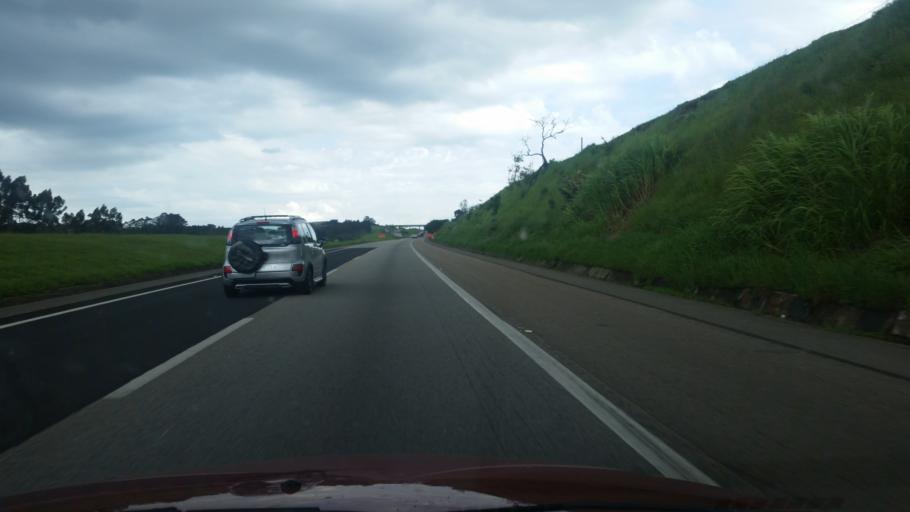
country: BR
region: Sao Paulo
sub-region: Itu
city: Itu
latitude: -23.3895
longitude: -47.3675
